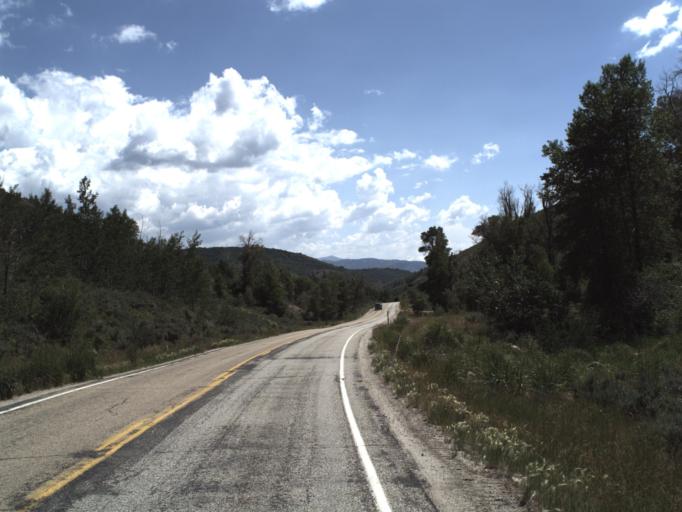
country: US
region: Utah
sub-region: Weber County
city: Wolf Creek
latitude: 41.3689
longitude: -111.5905
